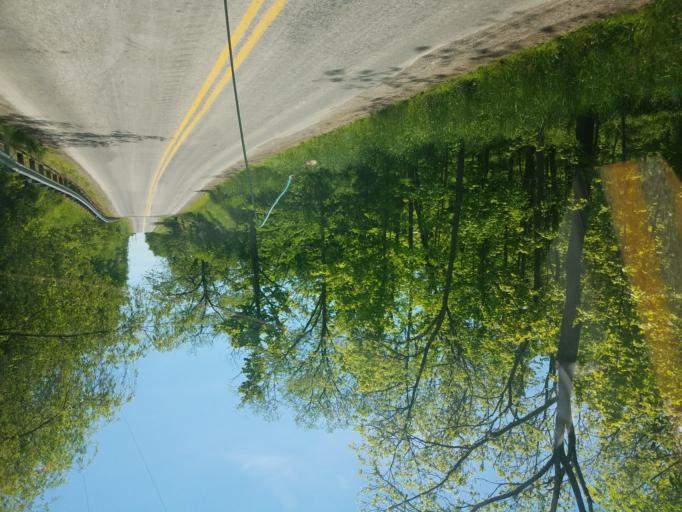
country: US
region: Ohio
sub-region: Ashland County
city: Ashland
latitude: 40.9589
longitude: -82.2438
